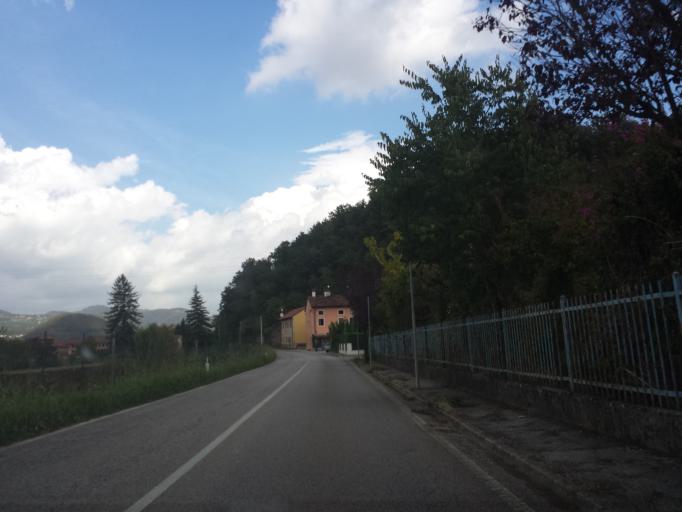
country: IT
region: Veneto
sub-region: Provincia di Vicenza
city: Gambugliano
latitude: 45.5635
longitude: 11.4244
